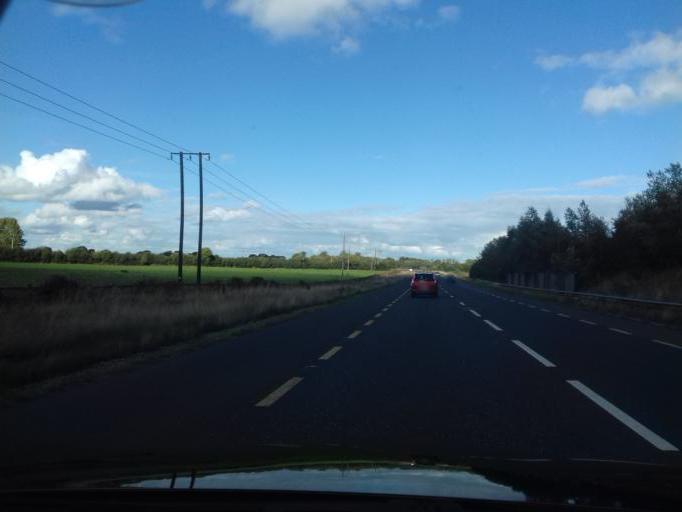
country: IE
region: Leinster
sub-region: Uibh Fhaili
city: Tullamore
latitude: 53.2555
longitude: -7.4750
